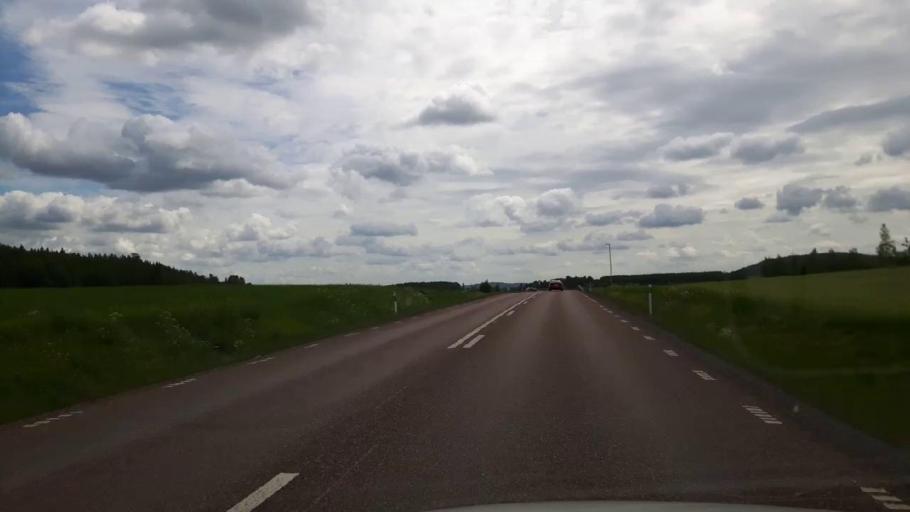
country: SE
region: Dalarna
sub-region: Hedemora Kommun
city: Hedemora
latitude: 60.3199
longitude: 15.9572
